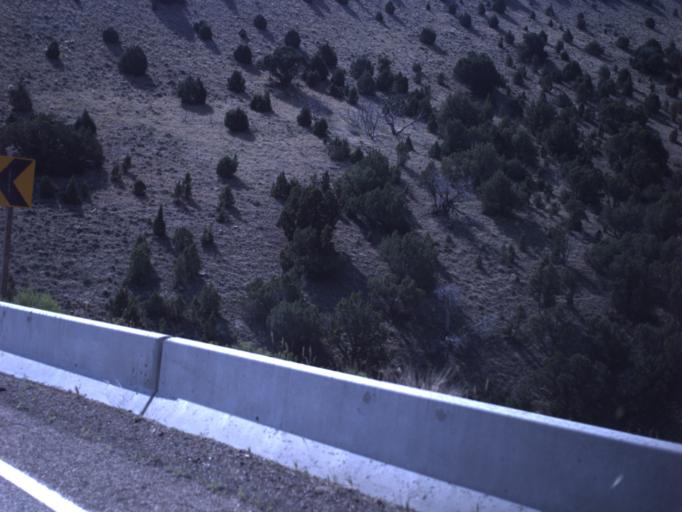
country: US
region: Utah
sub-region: Daggett County
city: Manila
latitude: 40.9124
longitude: -109.6835
